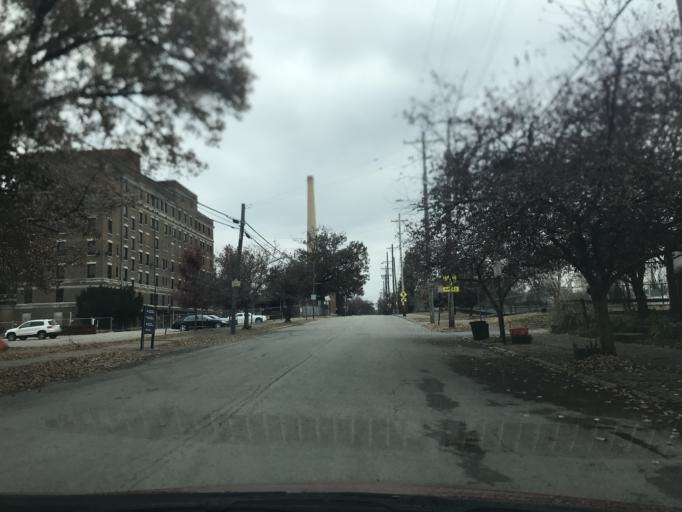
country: US
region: Kentucky
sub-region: Jefferson County
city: Louisville
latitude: 38.2412
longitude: -85.7342
